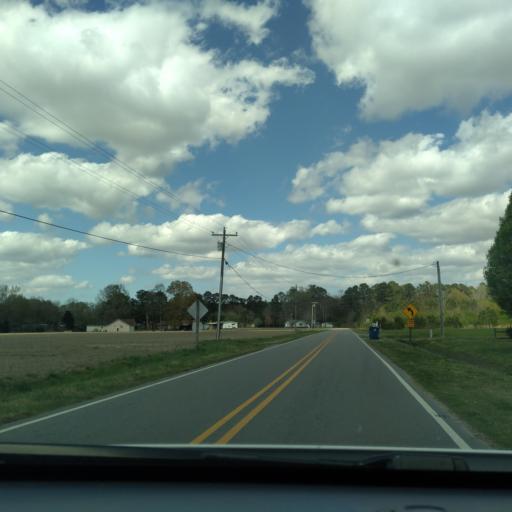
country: US
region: North Carolina
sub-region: Washington County
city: Plymouth
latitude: 35.8358
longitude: -76.7199
